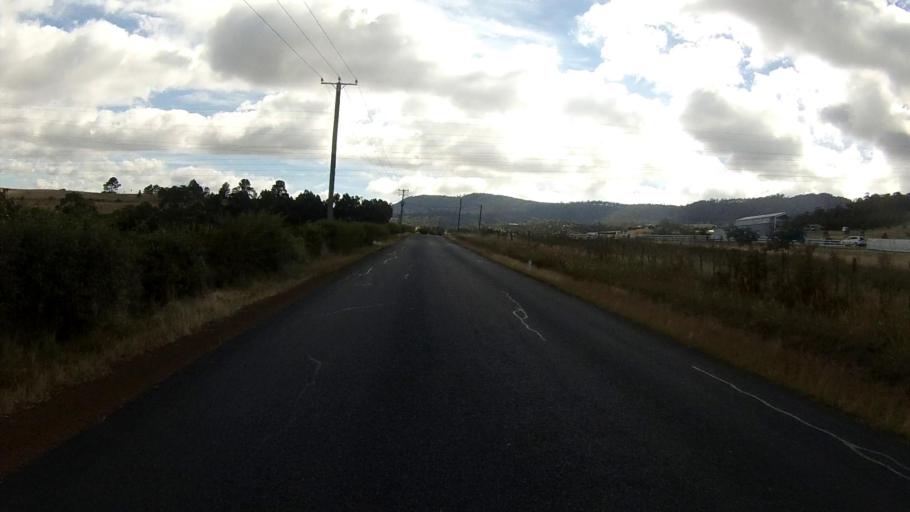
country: AU
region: Tasmania
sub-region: Brighton
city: Old Beach
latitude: -42.7698
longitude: 147.2943
